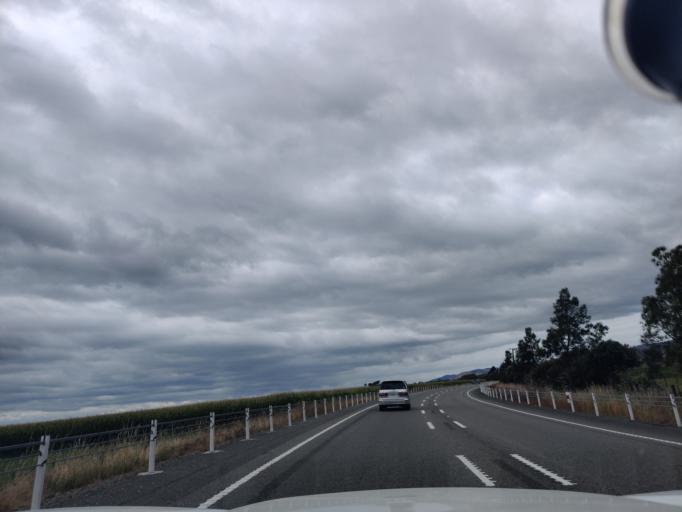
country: NZ
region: Manawatu-Wanganui
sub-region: Horowhenua District
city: Levin
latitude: -40.5806
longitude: 175.3592
